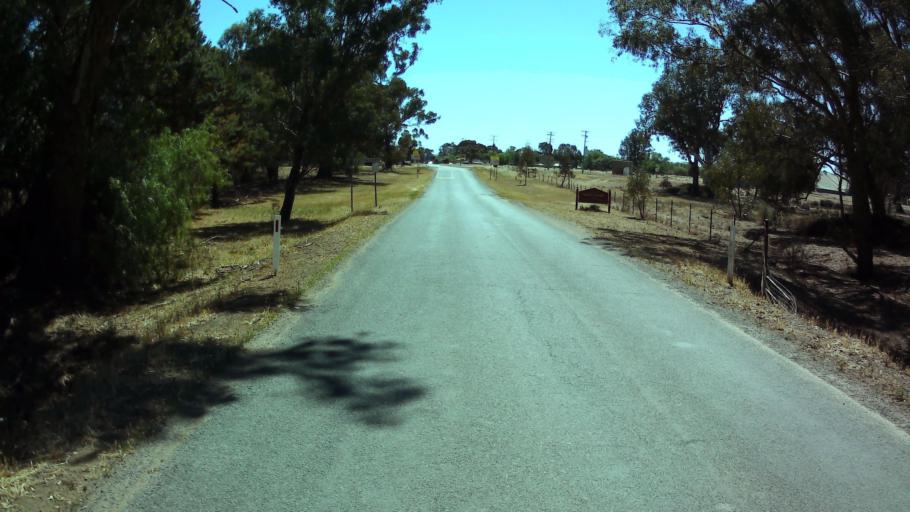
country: AU
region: New South Wales
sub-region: Weddin
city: Grenfell
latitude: -33.9991
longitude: 148.3986
